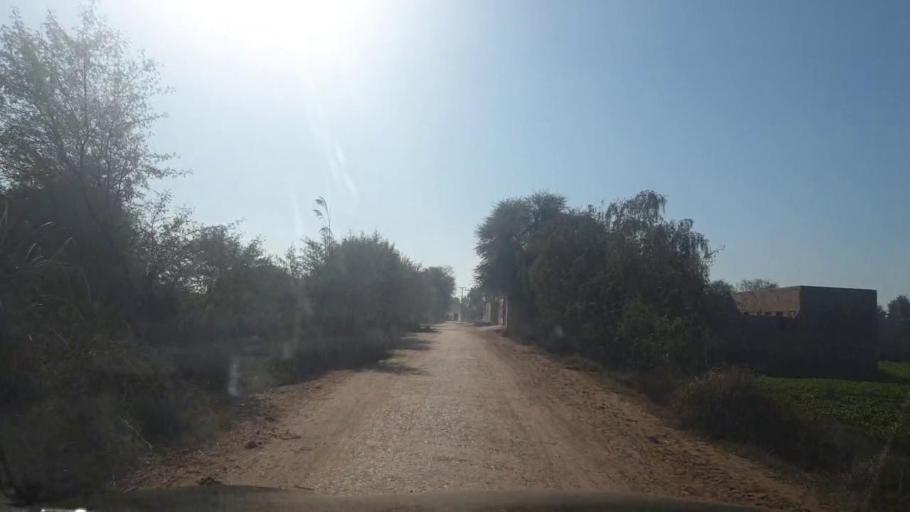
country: PK
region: Sindh
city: Ghotki
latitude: 27.9820
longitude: 69.3262
